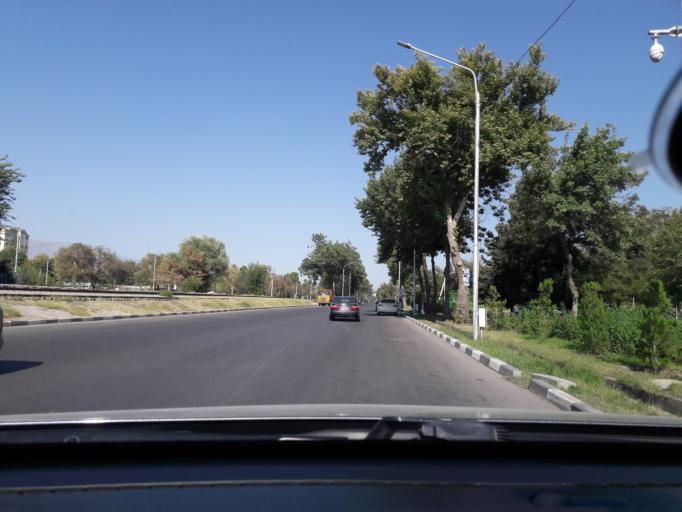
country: TJ
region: Dushanbe
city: Dushanbe
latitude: 38.5677
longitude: 68.7420
